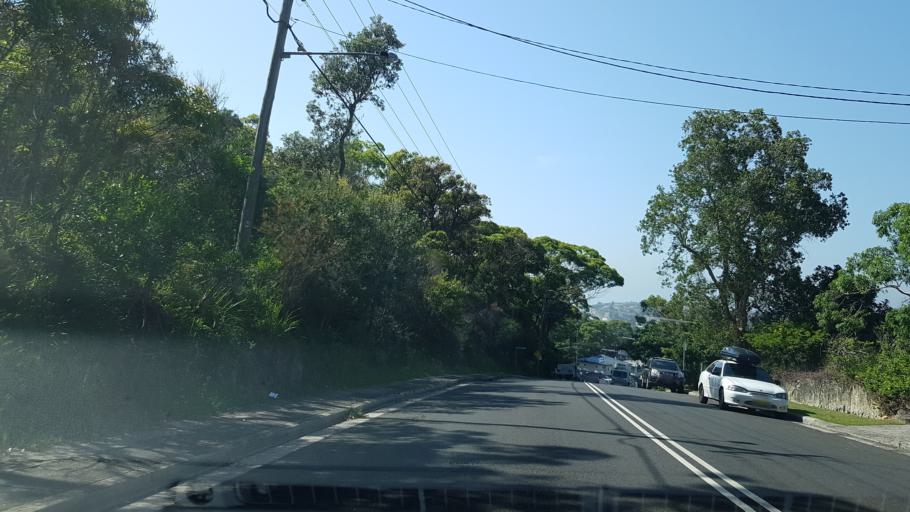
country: AU
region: New South Wales
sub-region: Warringah
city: Dee Why
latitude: -33.7376
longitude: 151.2908
